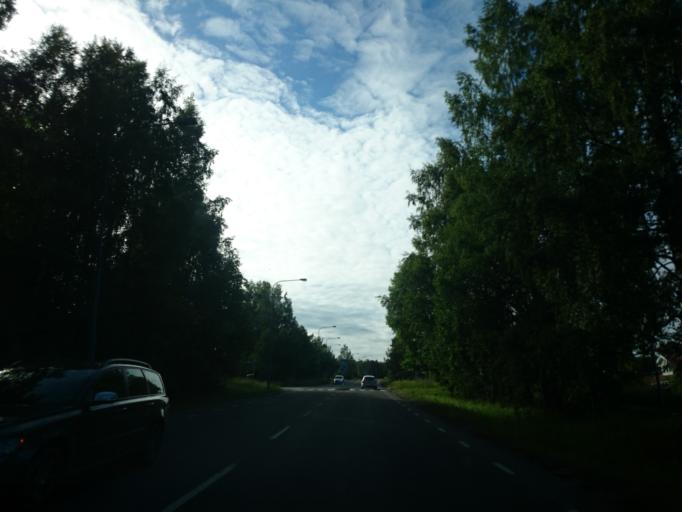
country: SE
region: Vaesternorrland
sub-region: Sundsvalls Kommun
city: Sundsvall
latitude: 62.4025
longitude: 17.3222
